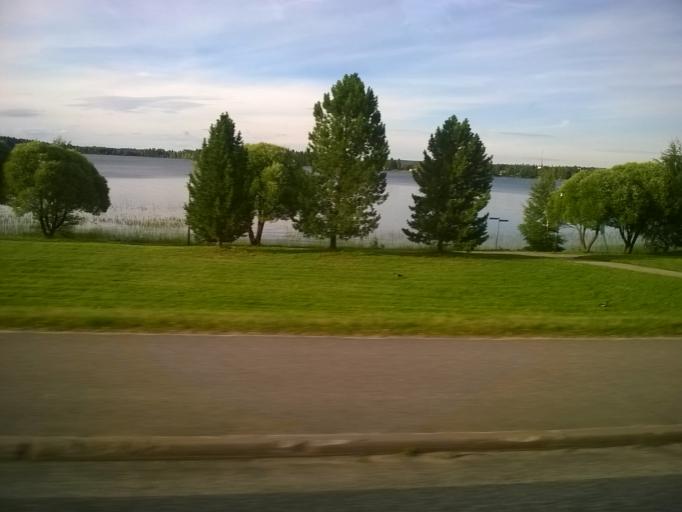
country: FI
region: Kainuu
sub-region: Kajaani
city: Sotkamo
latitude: 64.1292
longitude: 28.3716
